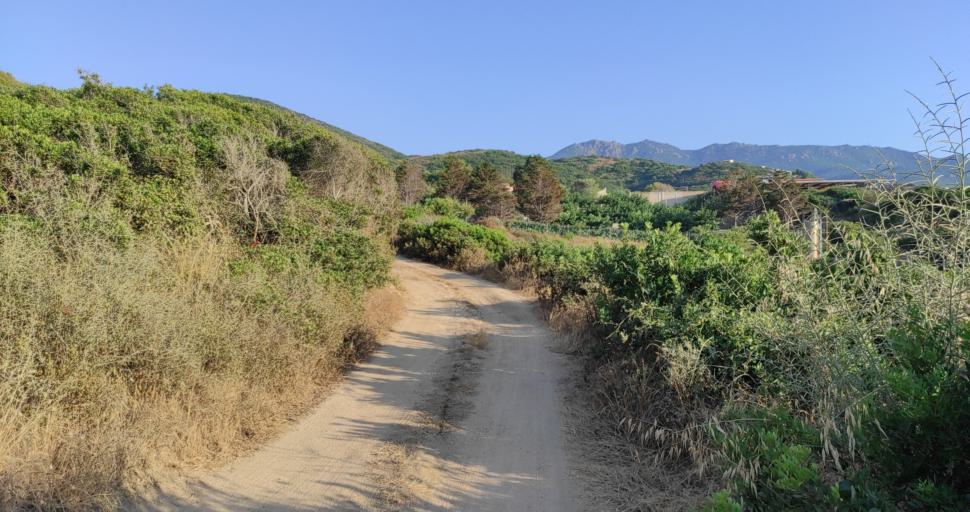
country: FR
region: Corsica
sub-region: Departement de la Corse-du-Sud
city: Alata
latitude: 41.9855
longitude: 8.6708
